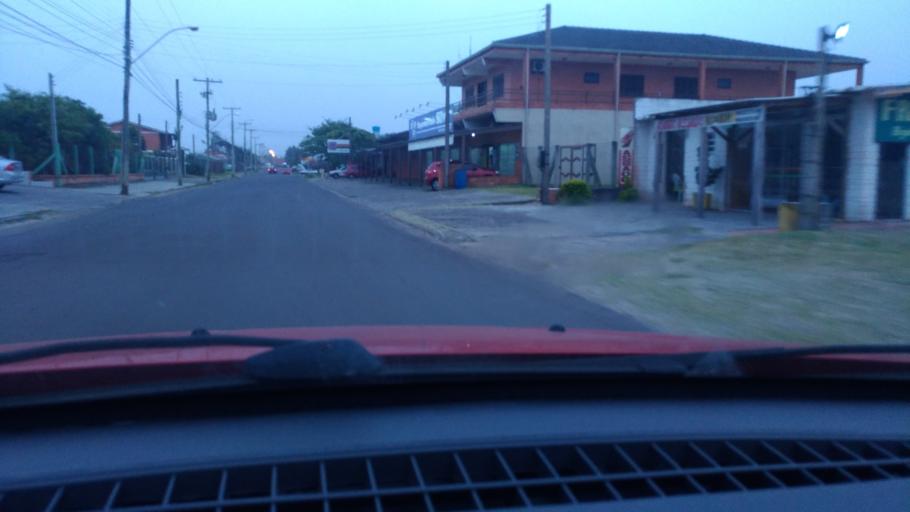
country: BR
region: Rio Grande do Sul
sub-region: Capao Da Canoa
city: Capao da Canoa
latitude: -29.8511
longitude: -50.0649
